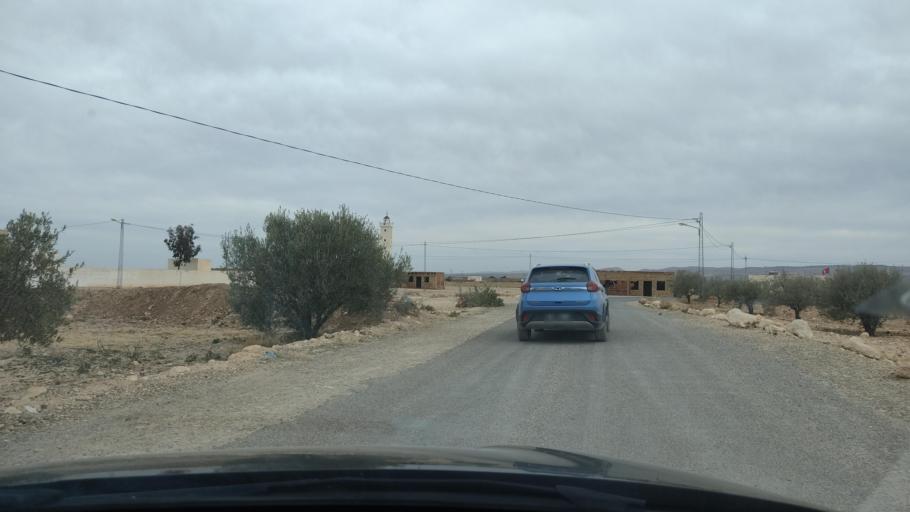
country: TN
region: Al Qasrayn
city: Kasserine
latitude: 35.2657
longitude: 8.9336
